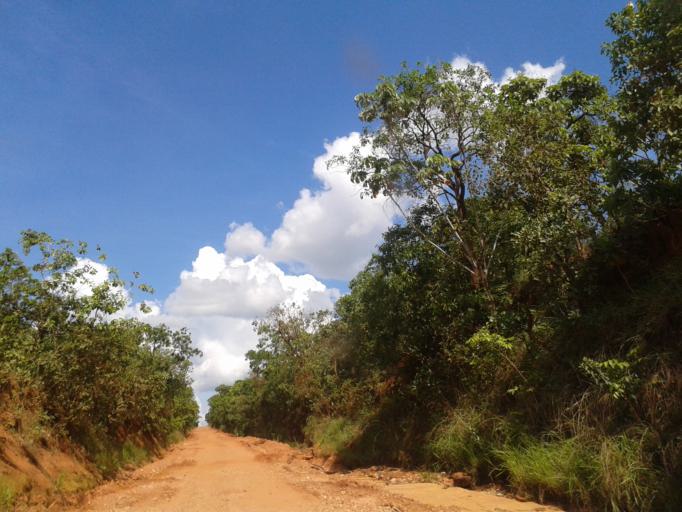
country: BR
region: Minas Gerais
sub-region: Campina Verde
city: Campina Verde
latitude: -19.3271
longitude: -49.7900
